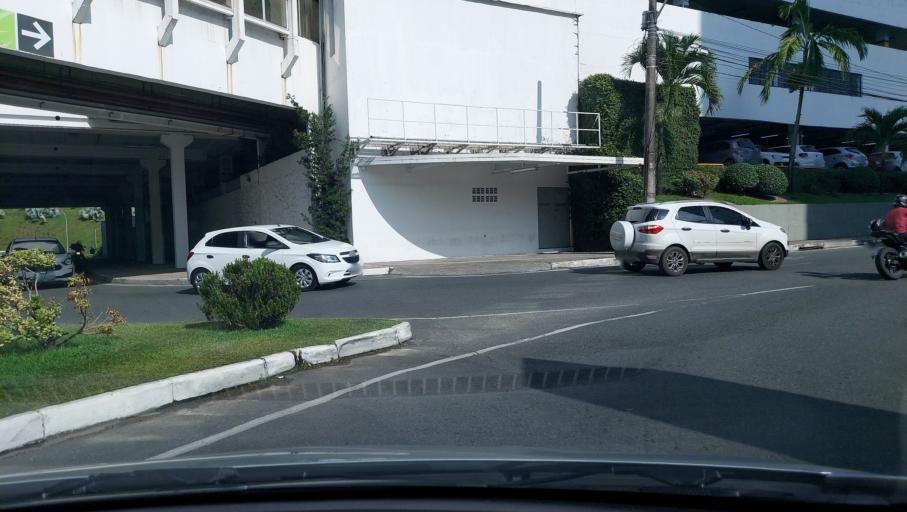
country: BR
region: Bahia
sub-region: Salvador
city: Salvador
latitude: -12.9828
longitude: -38.4645
